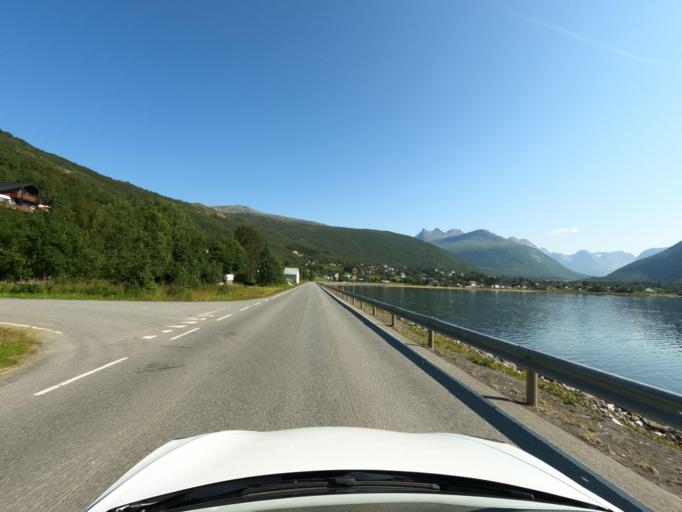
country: NO
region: Nordland
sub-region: Narvik
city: Bjerkvik
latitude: 68.3819
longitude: 17.5894
